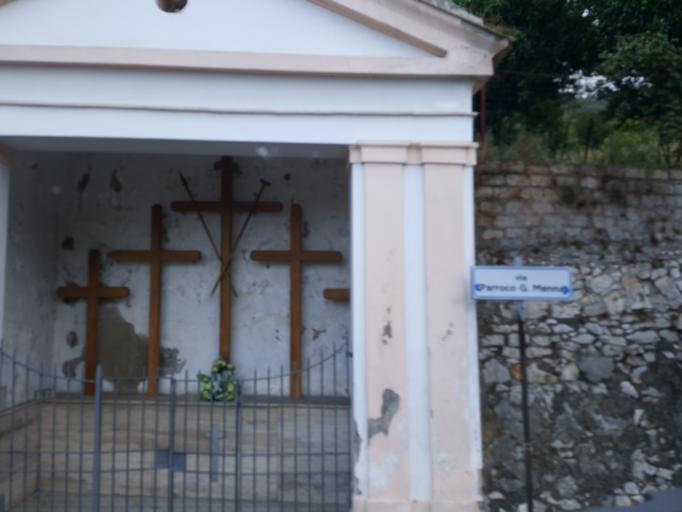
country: IT
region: Campania
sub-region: Provincia di Avellino
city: Domicella
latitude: 40.8782
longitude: 14.5838
